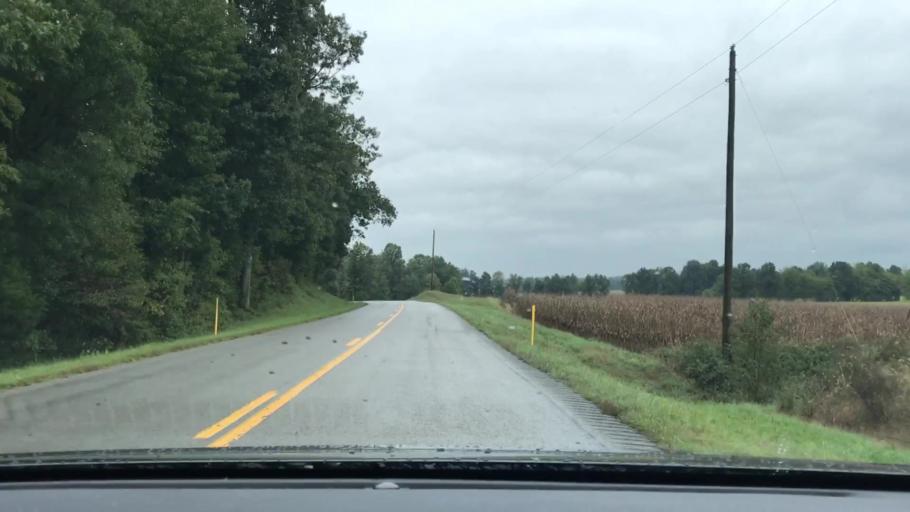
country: US
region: Kentucky
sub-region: McLean County
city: Calhoun
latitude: 37.4777
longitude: -87.2454
